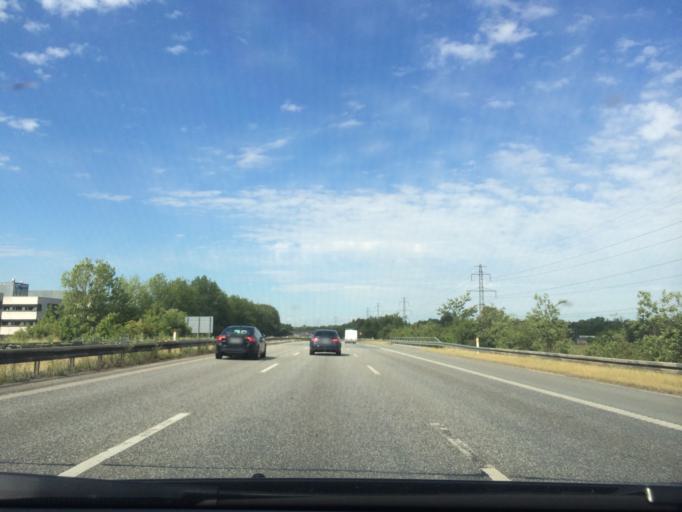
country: DK
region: Capital Region
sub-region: Vallensbaek Kommune
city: Vallensbaek
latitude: 55.6290
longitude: 12.3915
